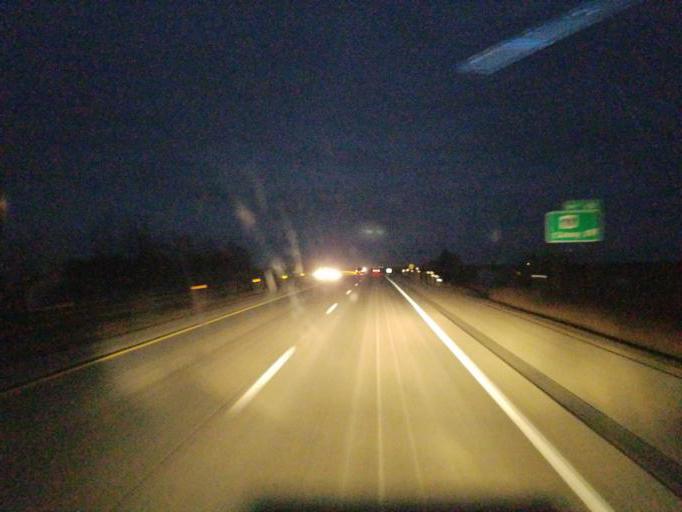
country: US
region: Iowa
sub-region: Guthrie County
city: Guthrie Center
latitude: 41.4961
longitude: -94.5265
